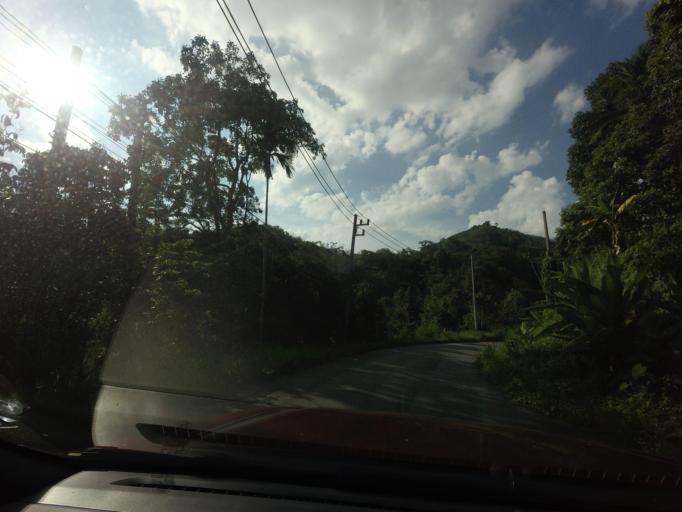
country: TH
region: Yala
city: Than To
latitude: 6.1397
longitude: 101.2973
